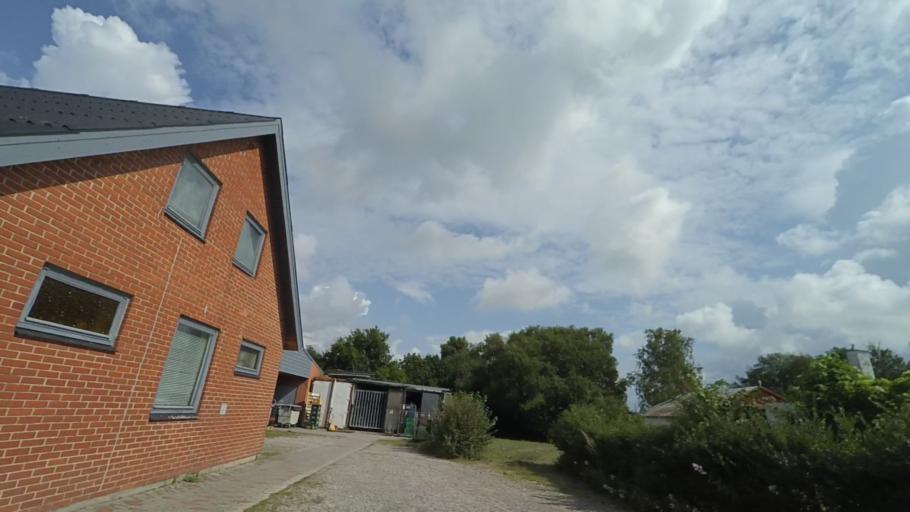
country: DK
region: Central Jutland
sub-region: Syddjurs Kommune
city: Ryomgard
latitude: 56.4772
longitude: 10.5057
